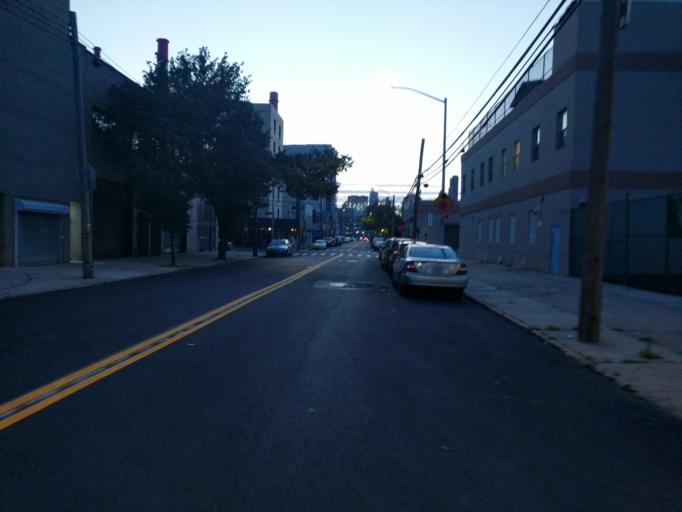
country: US
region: New York
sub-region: Queens County
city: Long Island City
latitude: 40.7595
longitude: -73.9401
